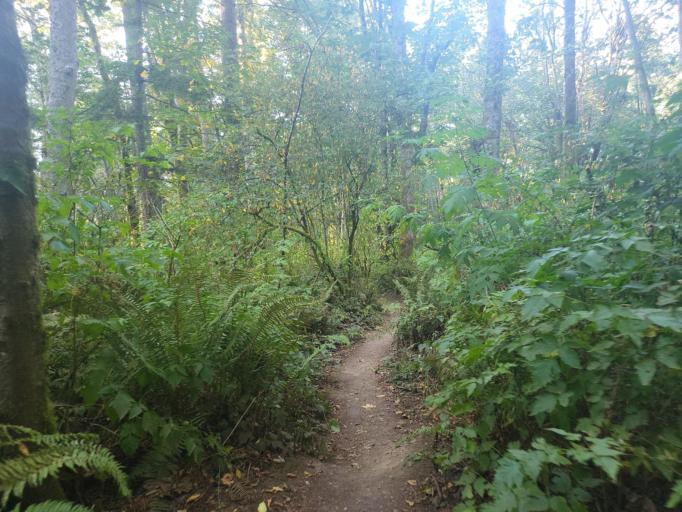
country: US
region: Washington
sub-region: Pierce County
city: Tacoma
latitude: 47.3126
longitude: -122.4084
